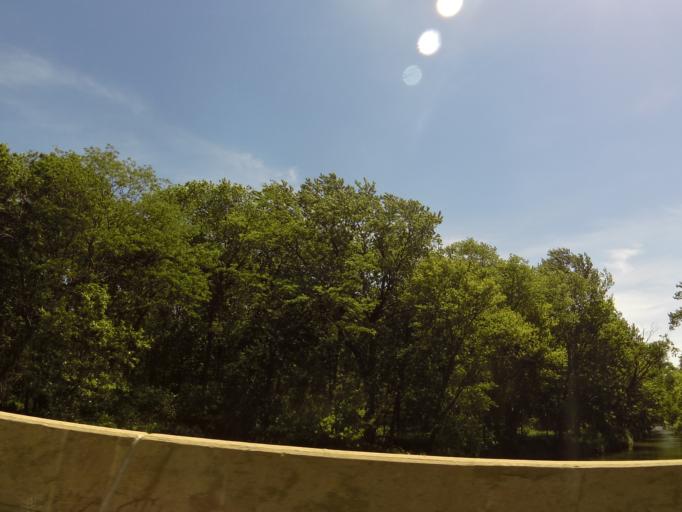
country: US
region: Illinois
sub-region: Vermilion County
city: Rossville
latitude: 40.3305
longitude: -87.6609
